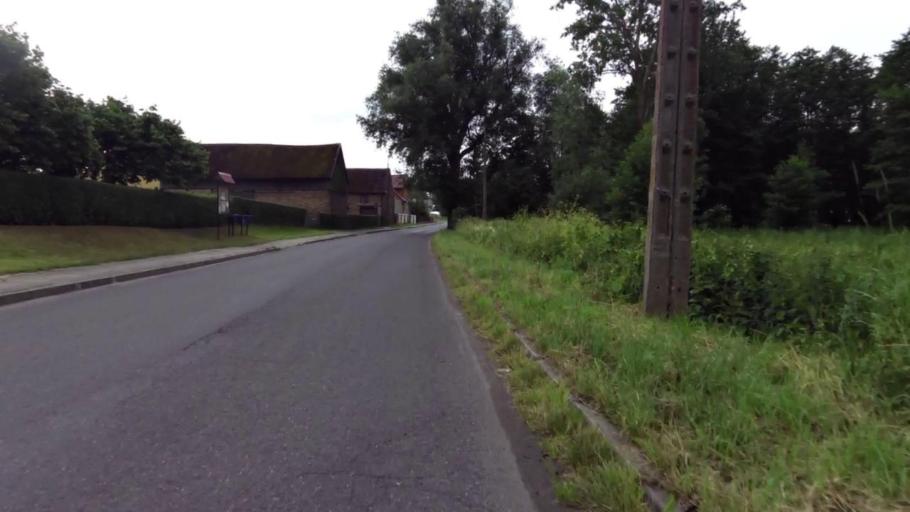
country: PL
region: West Pomeranian Voivodeship
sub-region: Powiat kamienski
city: Wolin
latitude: 53.8384
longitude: 14.6255
